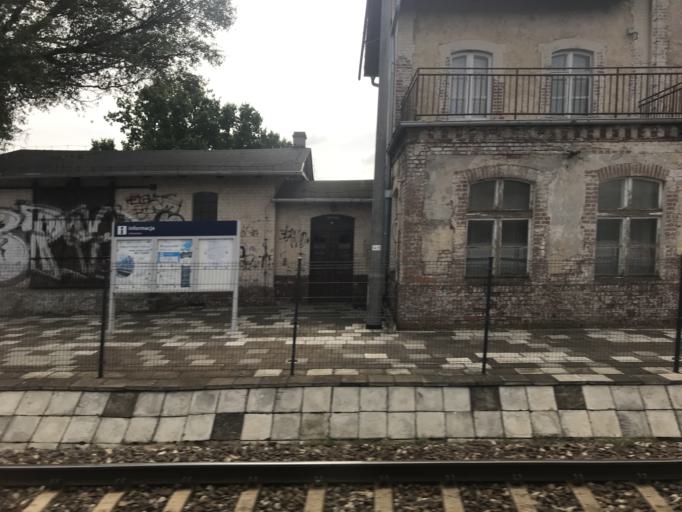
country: PL
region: Kujawsko-Pomorskie
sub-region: Powiat inowroclawski
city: Janikowo
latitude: 52.7130
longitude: 18.0349
